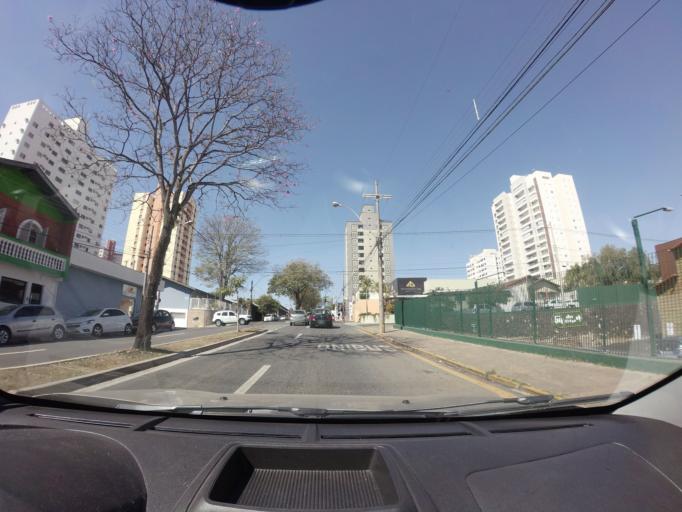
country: BR
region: Sao Paulo
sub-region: Piracicaba
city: Piracicaba
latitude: -22.7234
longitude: -47.6351
